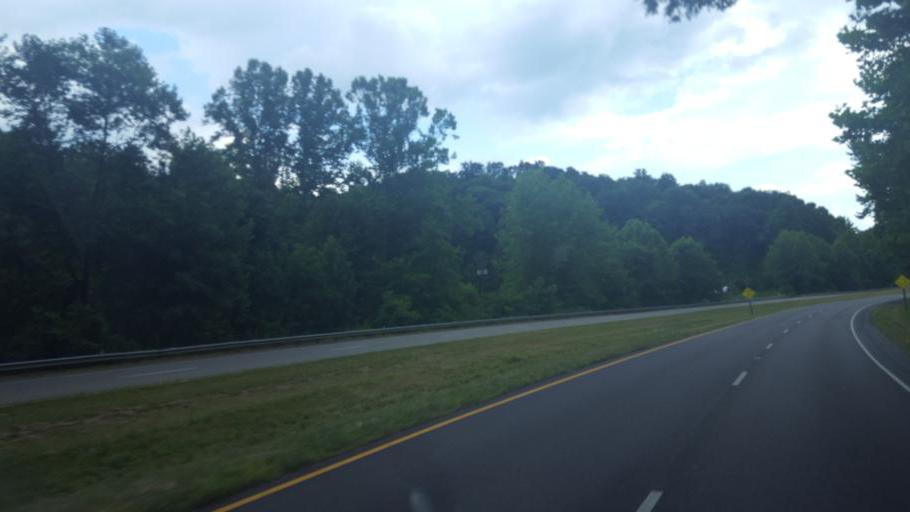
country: US
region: Virginia
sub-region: Wise County
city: Pound
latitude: 37.0744
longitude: -82.5991
